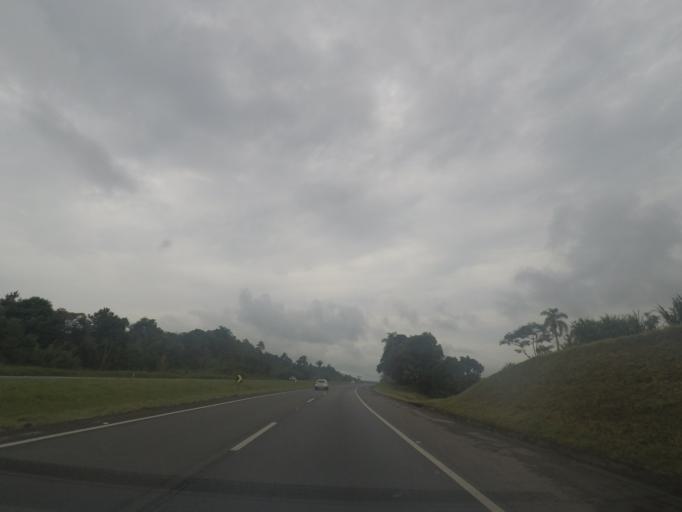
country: BR
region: Sao Paulo
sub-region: Cajati
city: Cajati
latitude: -24.9238
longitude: -48.2624
